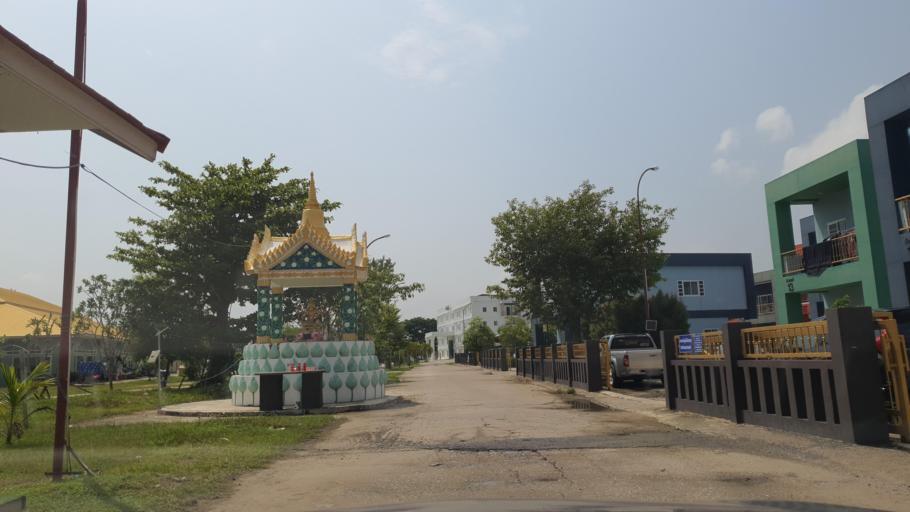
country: TH
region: Lamphun
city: Lamphun
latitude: 18.6035
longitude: 99.0132
